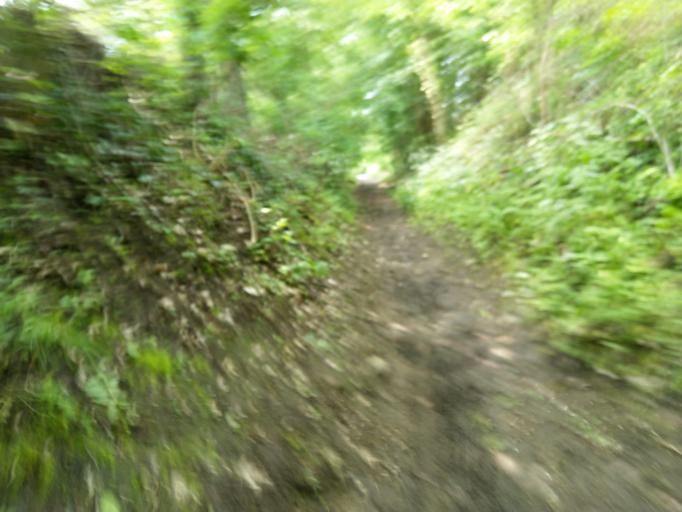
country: BE
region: Wallonia
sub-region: Province du Hainaut
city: Chasse Royale
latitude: 50.4362
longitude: 3.9700
